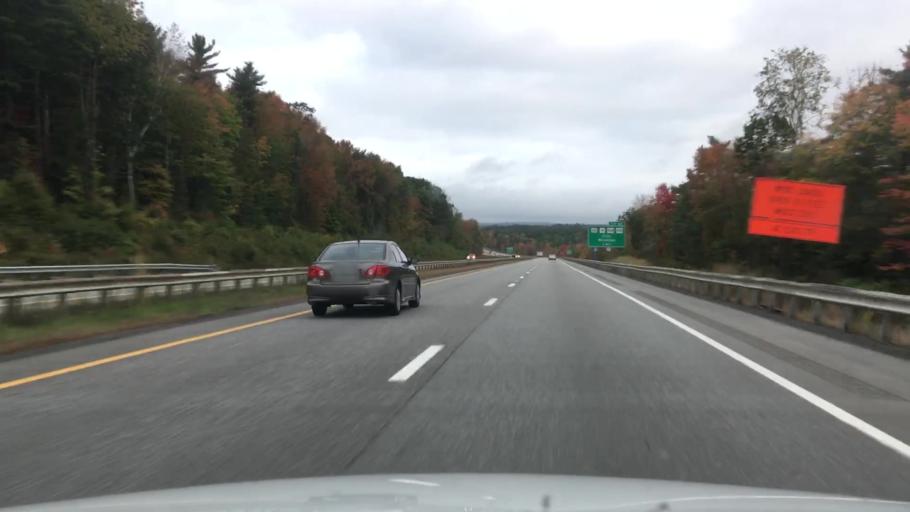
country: US
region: Maine
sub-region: Cumberland County
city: Cumberland Center
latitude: 43.8620
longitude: -70.3247
